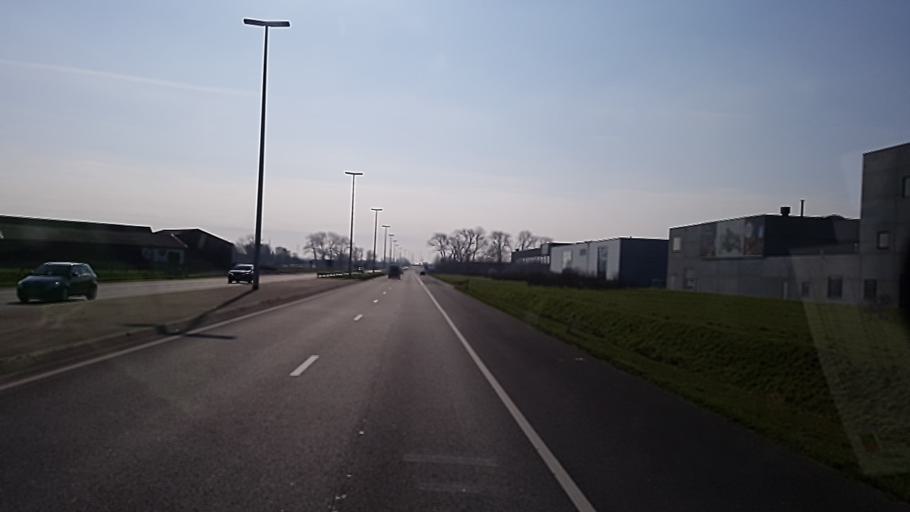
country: BE
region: Flanders
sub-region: Provincie West-Vlaanderen
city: Menen
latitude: 50.8158
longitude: 3.1279
